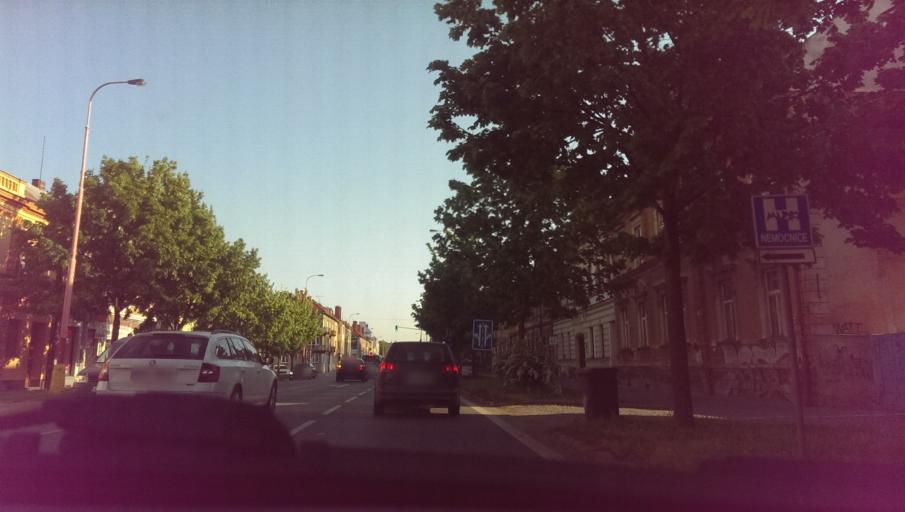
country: CZ
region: Zlin
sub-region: Okres Uherske Hradiste
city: Uherske Hradiste
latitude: 49.0649
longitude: 17.4665
